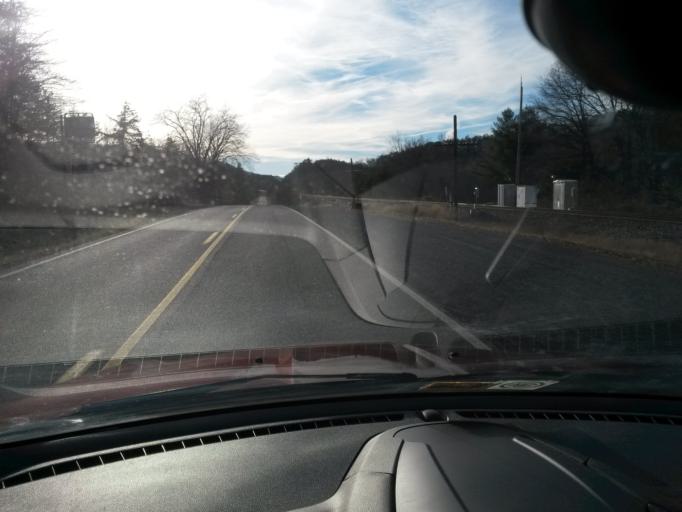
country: US
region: Virginia
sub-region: Alleghany County
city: Clifton Forge
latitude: 37.8452
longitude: -79.7488
